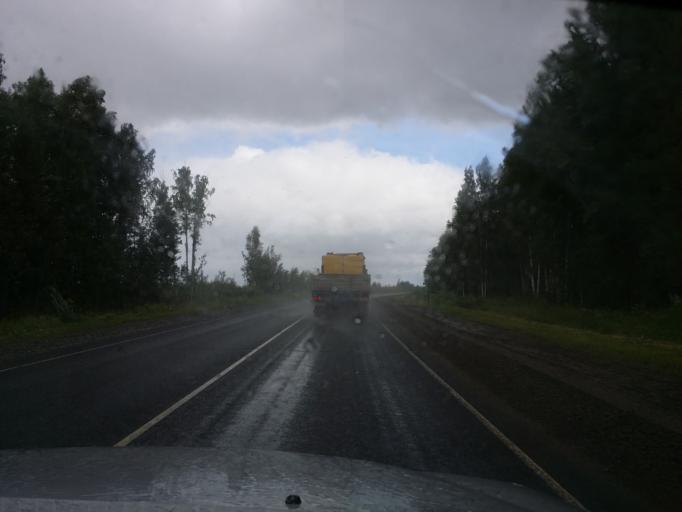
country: RU
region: Tjumen
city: Tobol'sk
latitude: 58.4302
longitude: 68.4273
